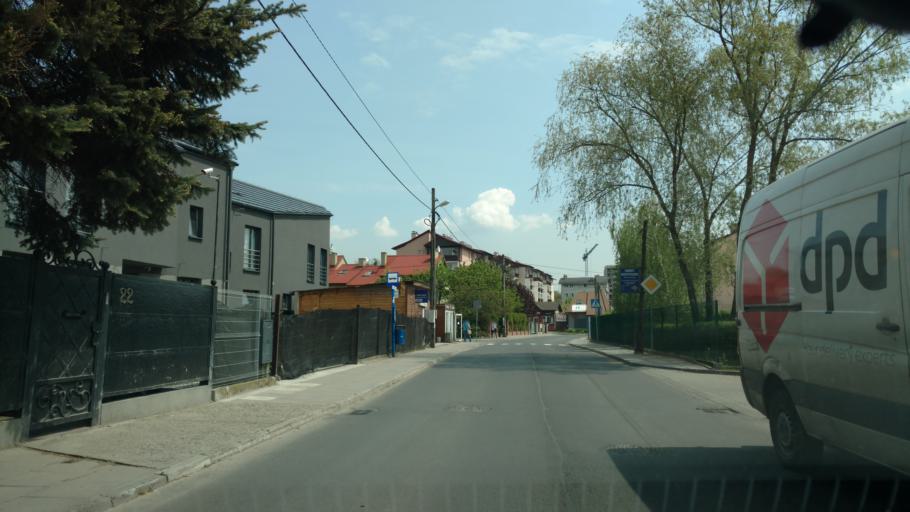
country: PL
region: Lesser Poland Voivodeship
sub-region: Krakow
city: Krakow
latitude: 50.0984
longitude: 19.9583
